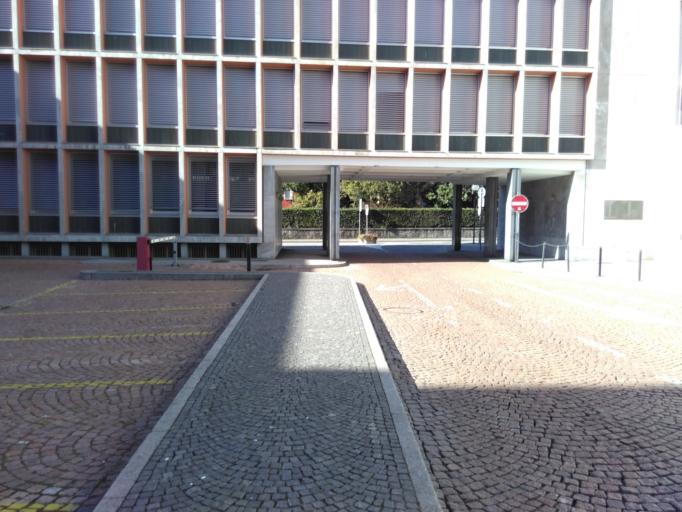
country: CH
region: Ticino
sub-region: Bellinzona District
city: Bellinzona
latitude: 46.1910
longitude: 9.0200
